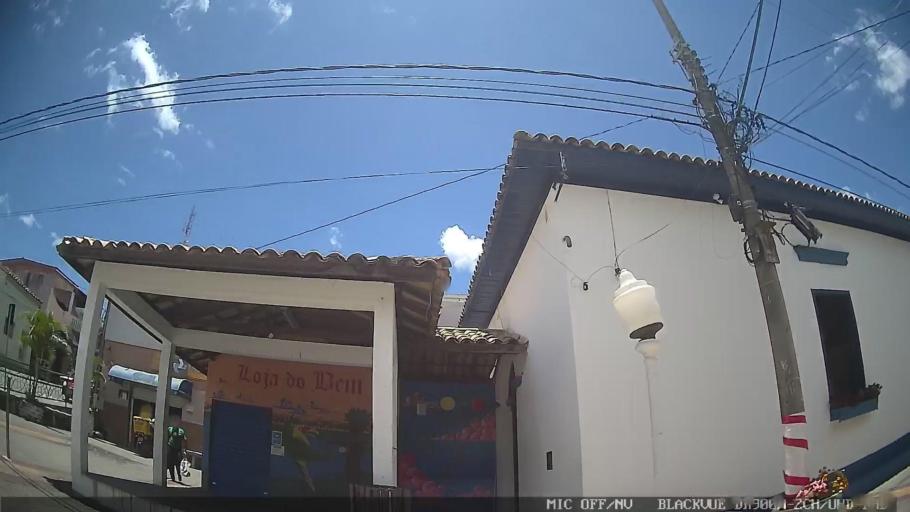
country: BR
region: Sao Paulo
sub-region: Santa Branca
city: Santa Branca
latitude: -23.5300
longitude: -45.8473
